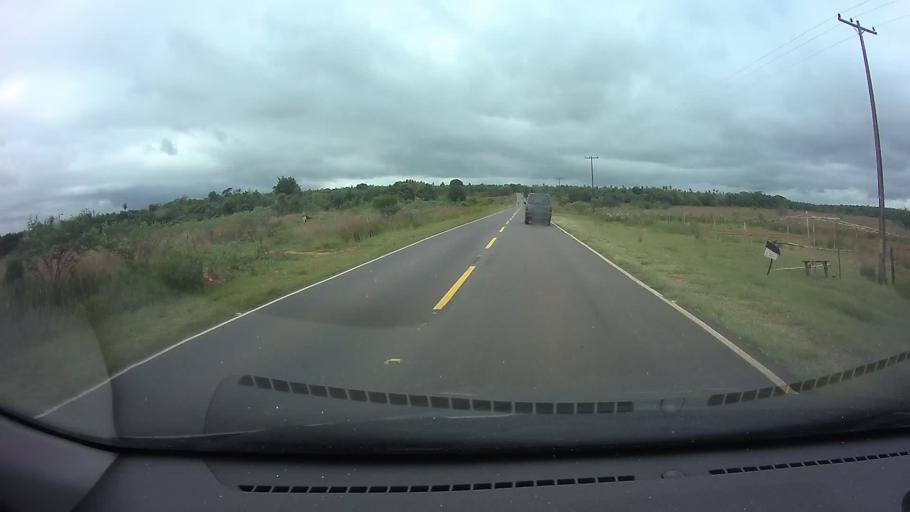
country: PY
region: Paraguari
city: Yaguaron
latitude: -25.7142
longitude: -57.3374
